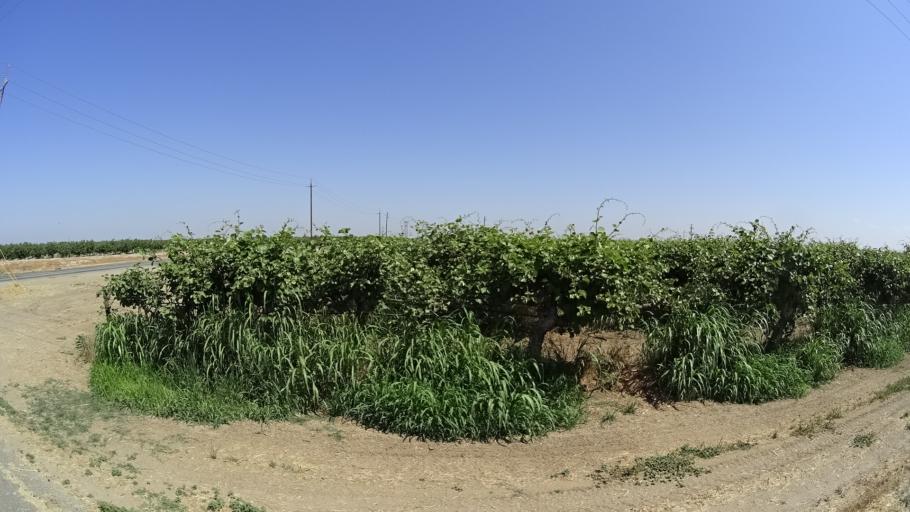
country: US
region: California
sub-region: Kings County
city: Hanford
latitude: 36.3719
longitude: -119.5826
